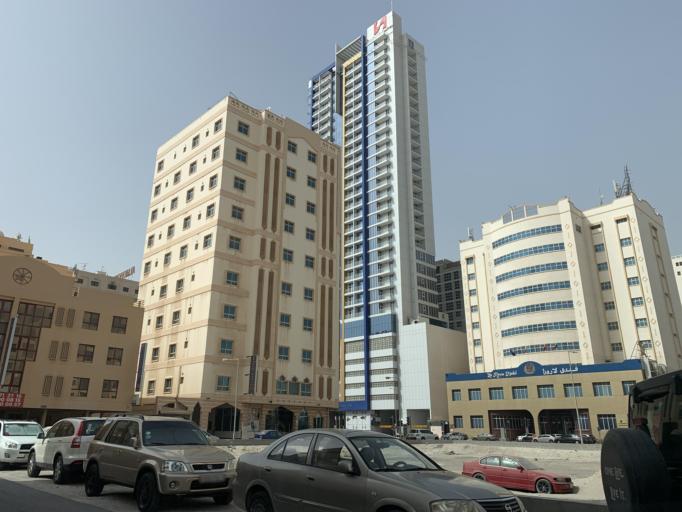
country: BH
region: Manama
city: Manama
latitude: 26.2125
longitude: 50.6107
